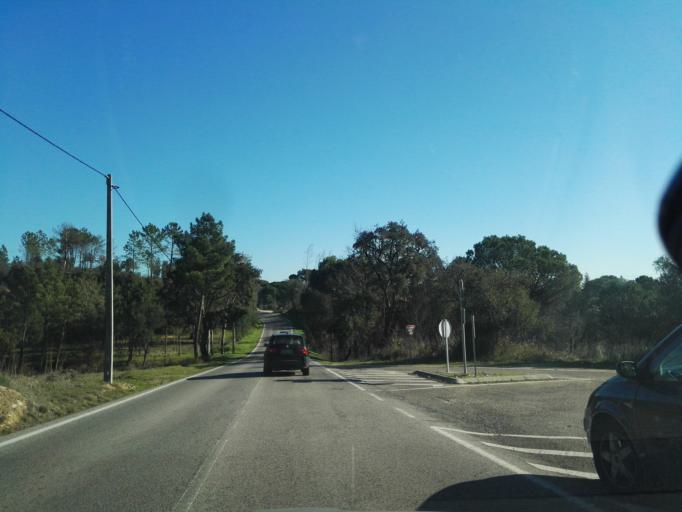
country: PT
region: Santarem
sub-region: Constancia
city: Constancia
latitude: 39.4815
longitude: -8.3220
